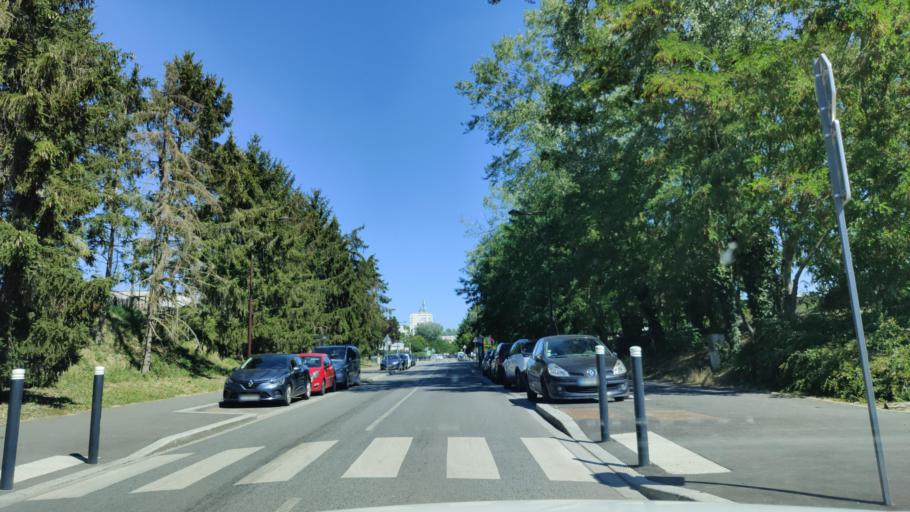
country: FR
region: Ile-de-France
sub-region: Departement de l'Essonne
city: Les Ulis
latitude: 48.6868
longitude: 2.1721
